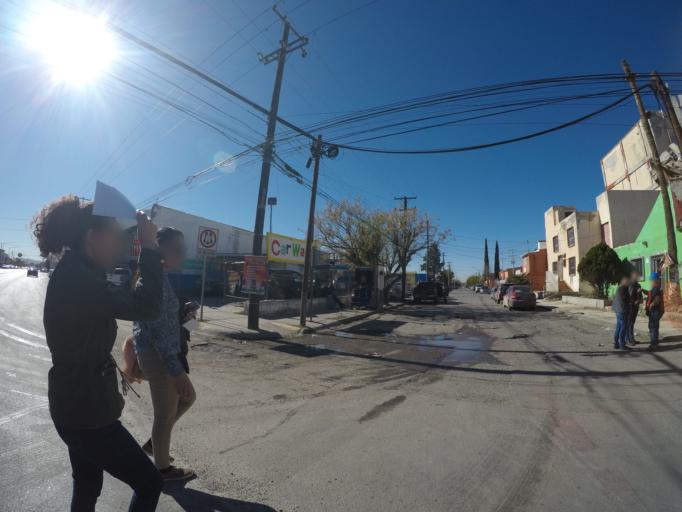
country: MX
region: Chihuahua
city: Ciudad Juarez
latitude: 31.7430
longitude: -106.4572
